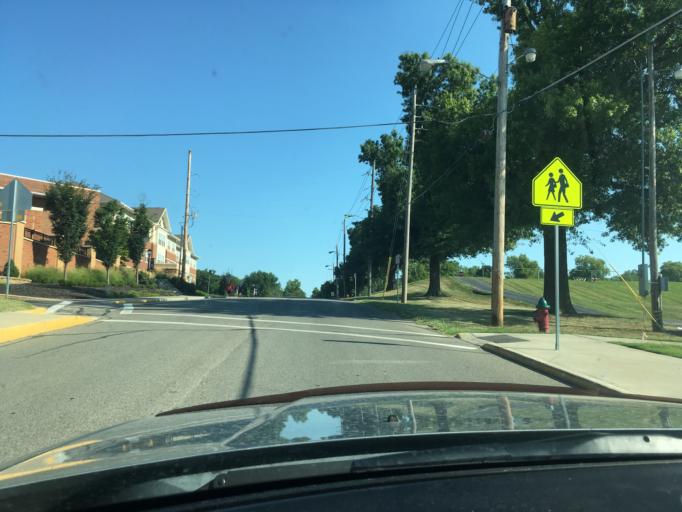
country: US
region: Kansas
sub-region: Atchison County
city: Atchison
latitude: 39.5762
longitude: -95.1152
